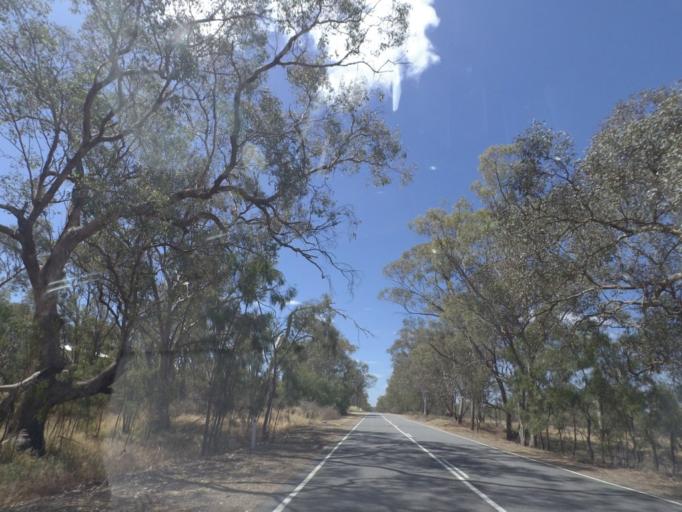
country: AU
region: Victoria
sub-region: Wangaratta
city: Wangaratta
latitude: -36.4452
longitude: 146.2423
